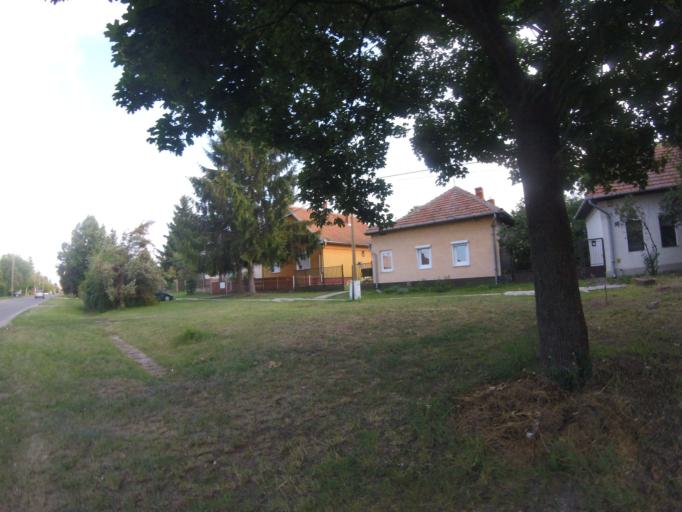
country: HU
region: Heves
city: Tiszanana
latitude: 47.5917
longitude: 20.5921
